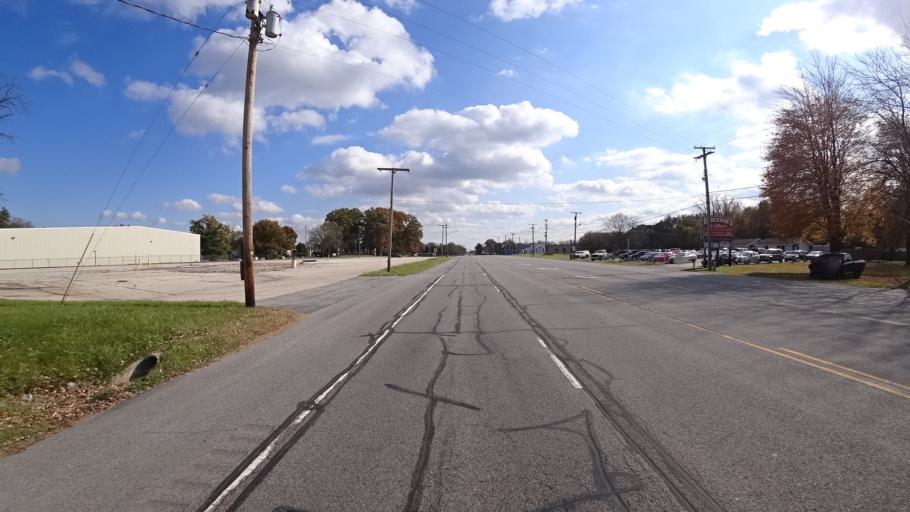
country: US
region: Indiana
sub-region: LaPorte County
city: Trail Creek
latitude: 41.7039
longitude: -86.8499
